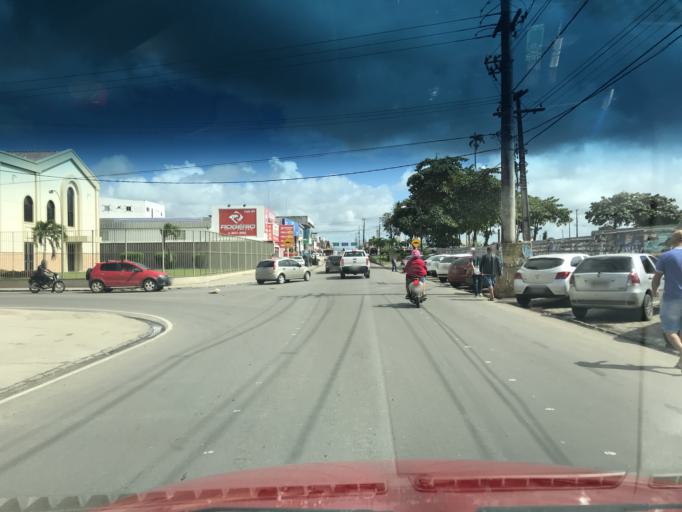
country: BR
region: Bahia
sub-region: Santo Antonio De Jesus
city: Santo Antonio de Jesus
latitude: -12.9652
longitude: -39.2689
